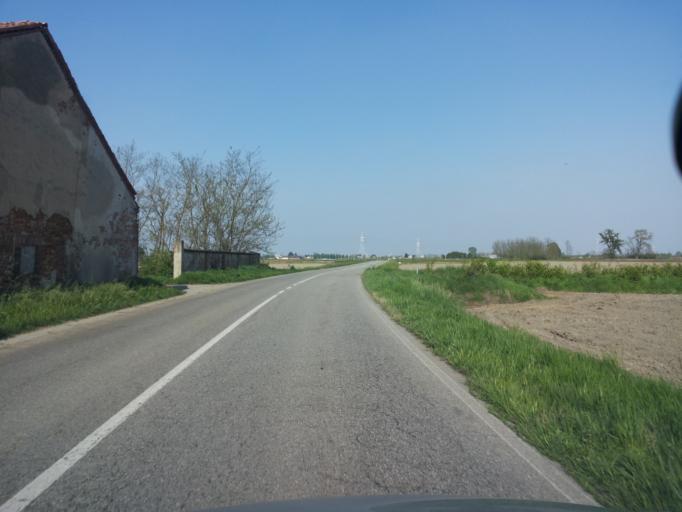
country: IT
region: Lombardy
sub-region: Provincia di Pavia
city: Zeme
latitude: 45.2201
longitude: 8.6624
